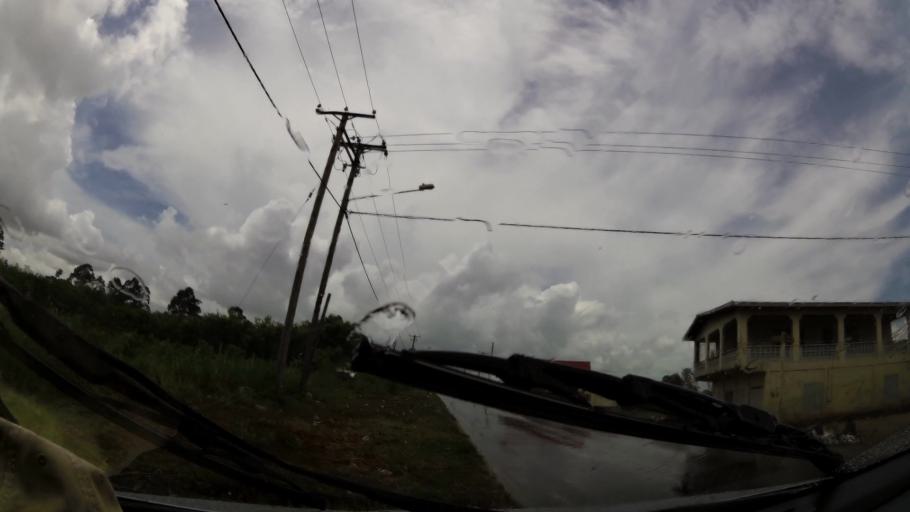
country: SR
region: Paramaribo
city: Paramaribo
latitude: 5.7919
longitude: -55.2199
